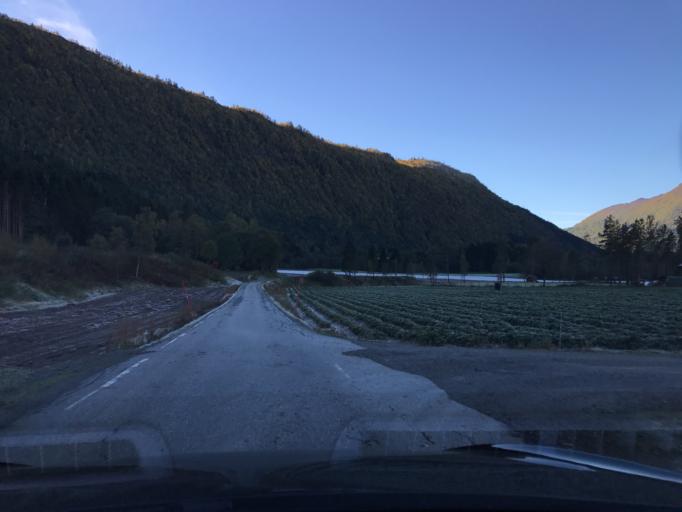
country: NO
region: More og Romsdal
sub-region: Norddal
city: Valldal
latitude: 62.3190
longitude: 7.3230
